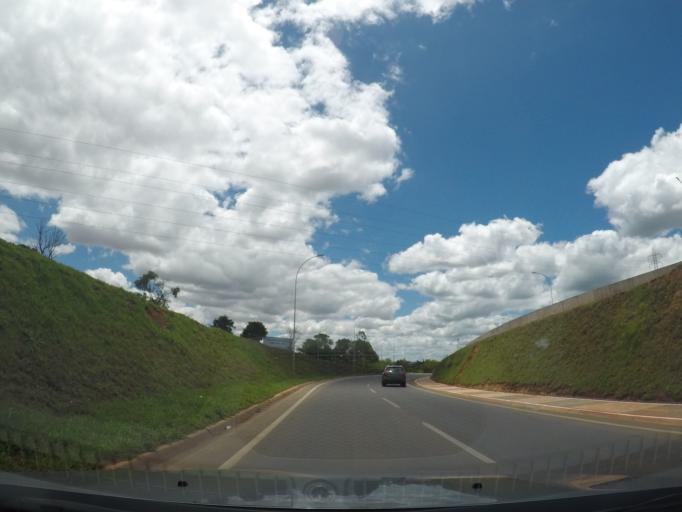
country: BR
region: Federal District
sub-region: Brasilia
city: Brasilia
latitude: -15.7248
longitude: -47.8977
